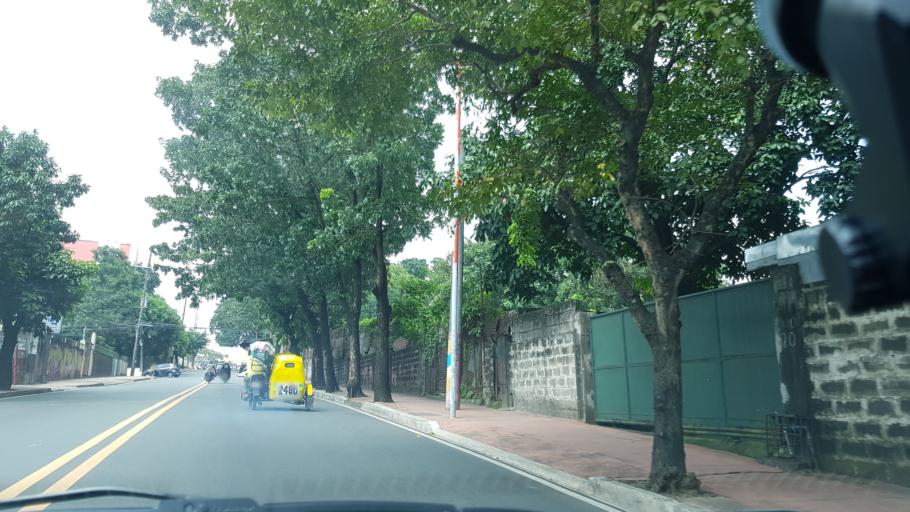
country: PH
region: Calabarzon
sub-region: Province of Rizal
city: Antipolo
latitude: 14.6584
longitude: 121.1185
